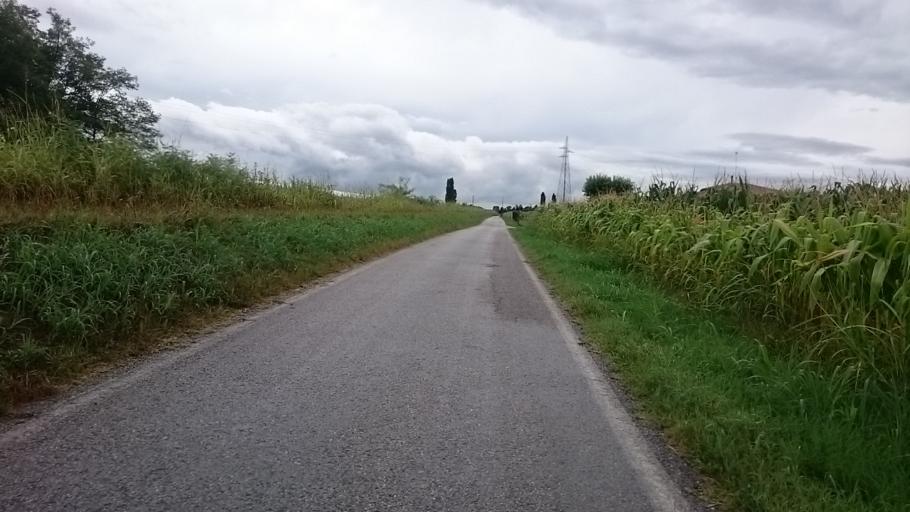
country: IT
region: Veneto
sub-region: Provincia di Treviso
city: Sant'Andrea
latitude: 45.6392
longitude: 11.9238
